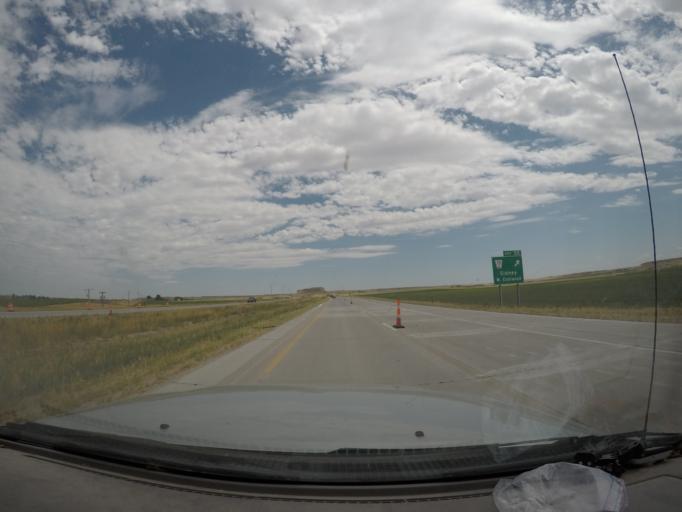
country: US
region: Nebraska
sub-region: Cheyenne County
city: Sidney
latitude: 41.1301
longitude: -103.0411
